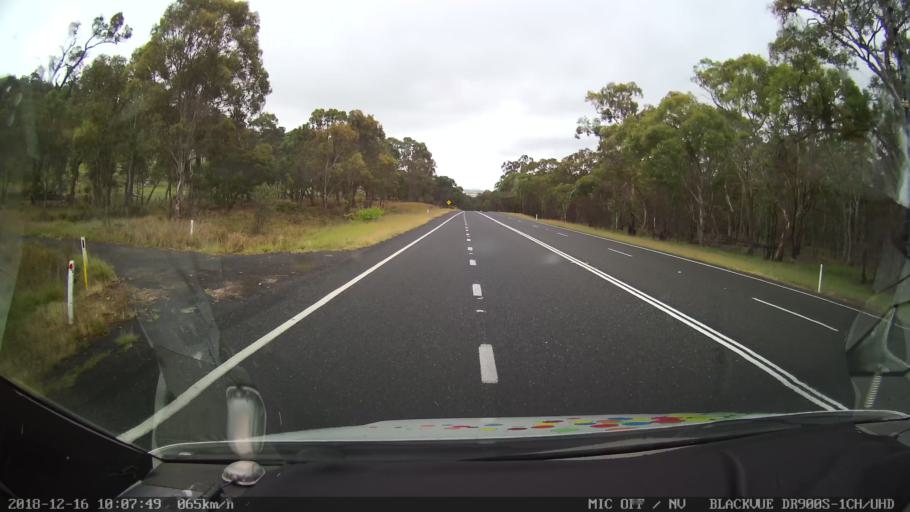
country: AU
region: New South Wales
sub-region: Glen Innes Severn
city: Glen Innes
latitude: -29.3334
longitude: 151.8994
